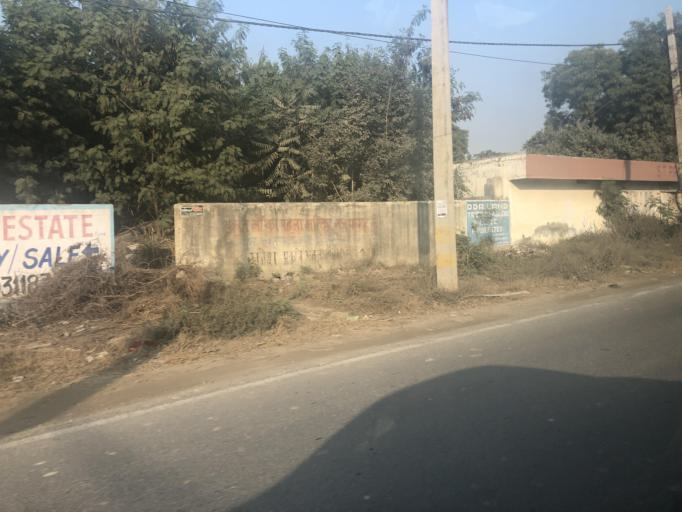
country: IN
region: Haryana
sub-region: Gurgaon
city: Gurgaon
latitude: 28.5383
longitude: 77.0347
